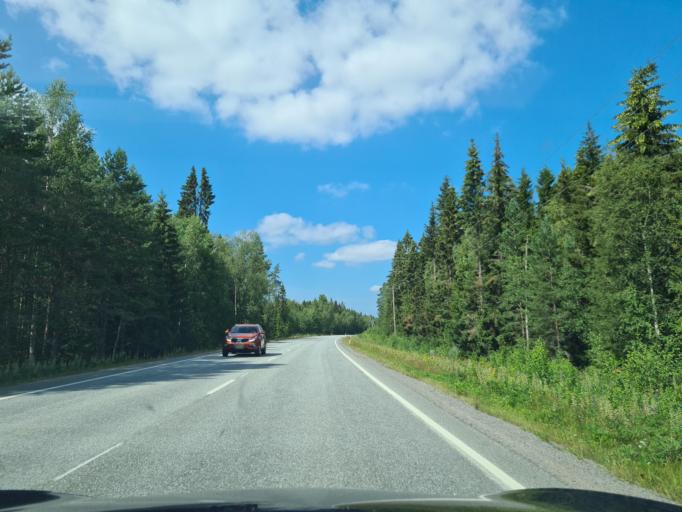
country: FI
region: Ostrobothnia
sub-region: Vaasa
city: Vaasa
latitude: 63.1721
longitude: 21.5812
